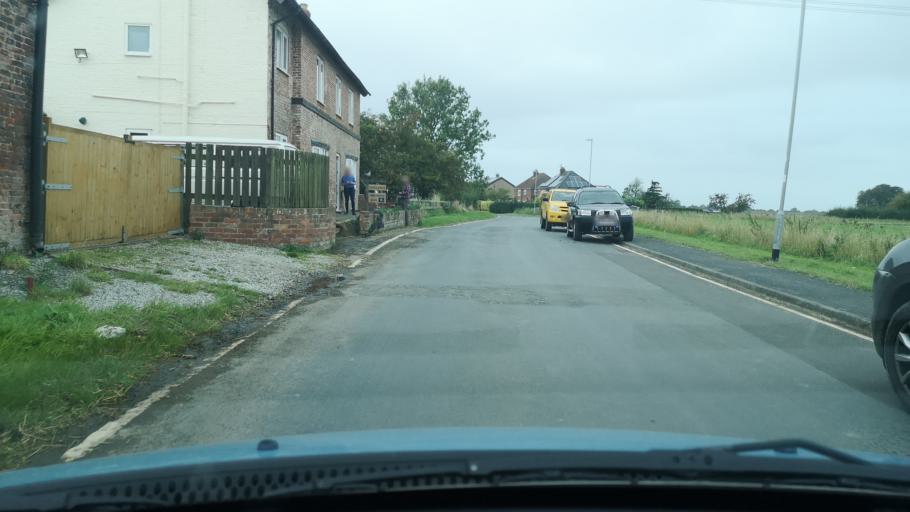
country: GB
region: England
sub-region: East Riding of Yorkshire
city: Laxton
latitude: 53.6982
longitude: -0.7452
